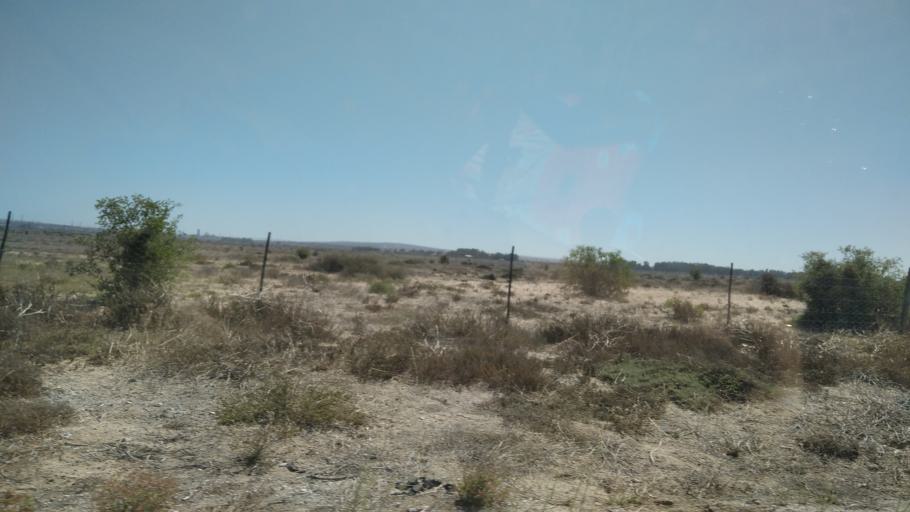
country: ZA
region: Western Cape
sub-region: West Coast District Municipality
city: Vredenburg
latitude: -33.0197
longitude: 18.1105
